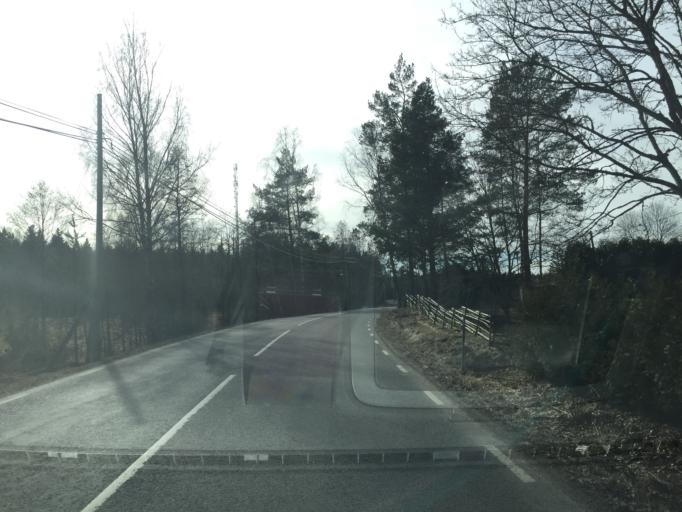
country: SE
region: Stockholm
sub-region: Haninge Kommun
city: Jordbro
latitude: 59.1156
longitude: 18.0145
